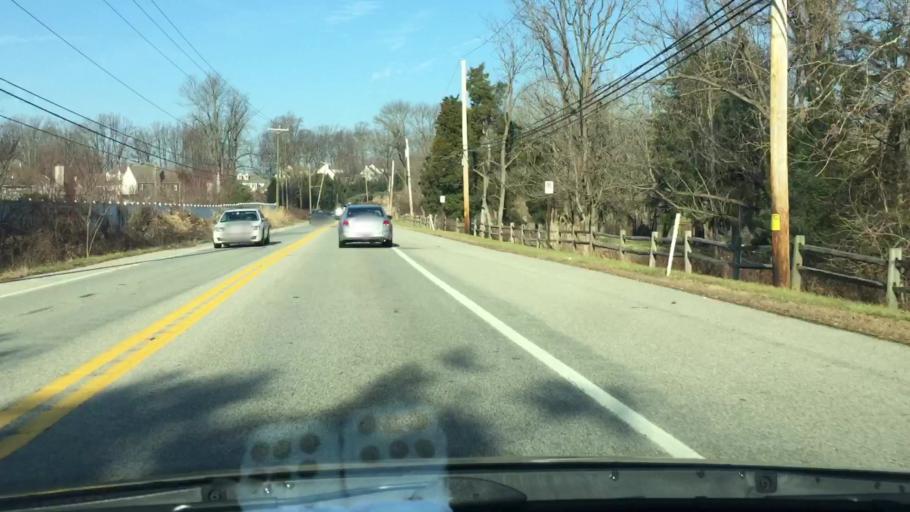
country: US
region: Pennsylvania
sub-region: Delaware County
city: Broomall
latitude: 39.9626
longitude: -75.3957
